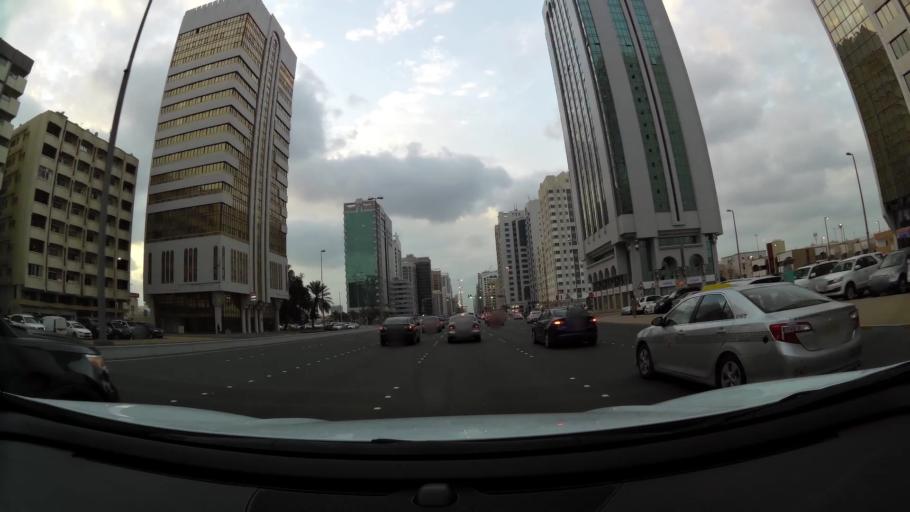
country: AE
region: Abu Dhabi
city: Abu Dhabi
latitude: 24.4622
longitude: 54.3784
